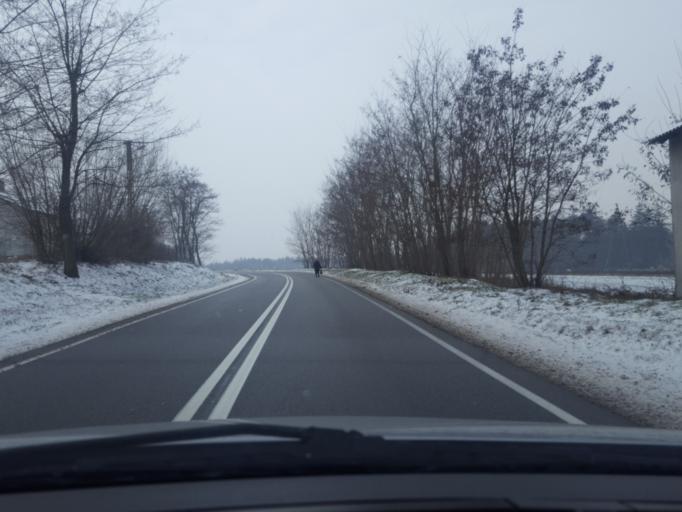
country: PL
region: Lodz Voivodeship
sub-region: Powiat brzezinski
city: Rogow
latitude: 51.8651
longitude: 19.8293
